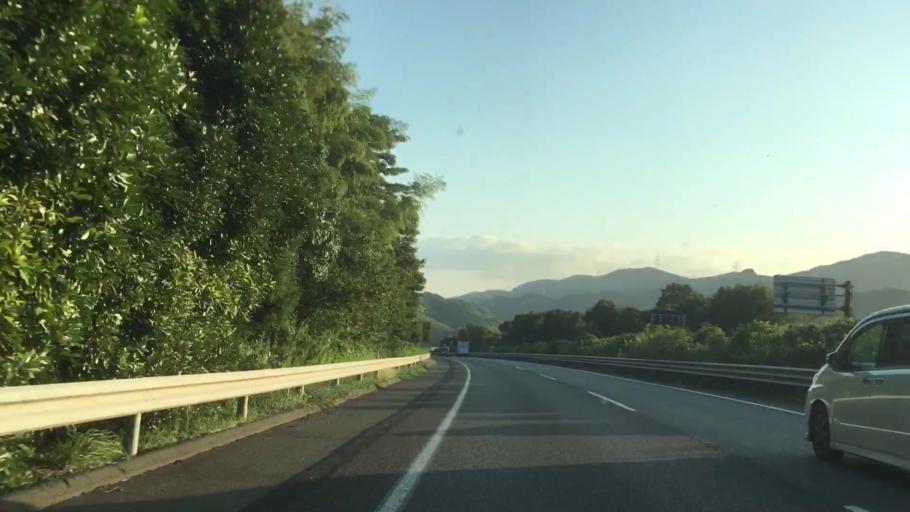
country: JP
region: Yamaguchi
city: Shimonoseki
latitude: 33.9152
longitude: 130.9764
